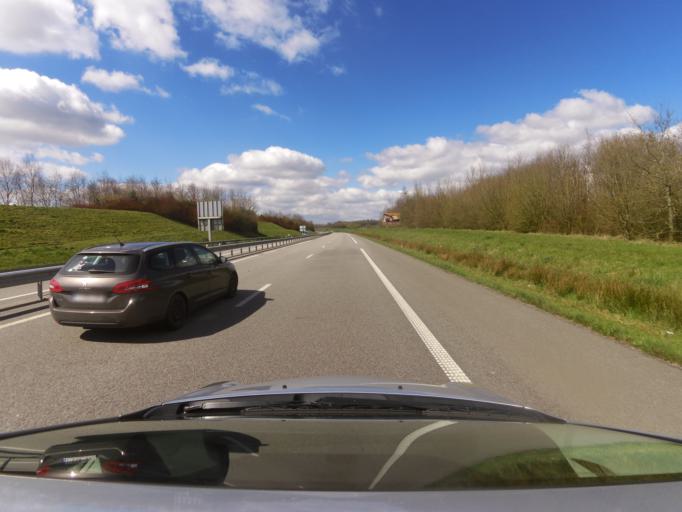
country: FR
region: Haute-Normandie
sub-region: Departement de la Seine-Maritime
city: Totes
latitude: 49.6413
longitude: 1.0206
